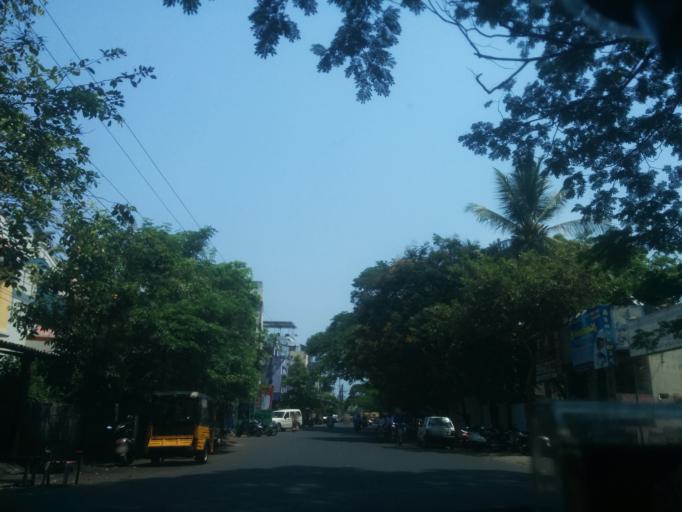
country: IN
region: Andhra Pradesh
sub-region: East Godavari
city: Rajahmundry
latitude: 17.0119
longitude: 81.7720
